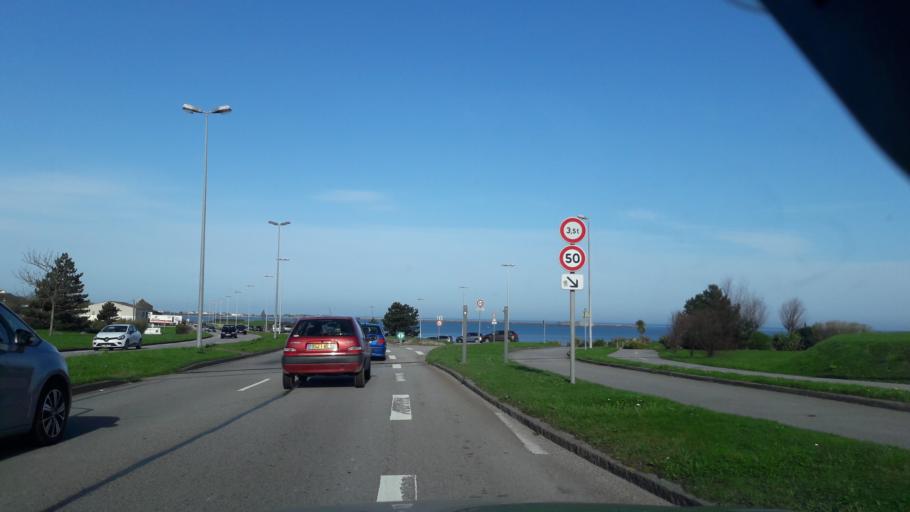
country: FR
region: Lower Normandy
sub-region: Departement de la Manche
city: Equeurdreville-Hainneville
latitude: 49.6551
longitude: -1.6502
